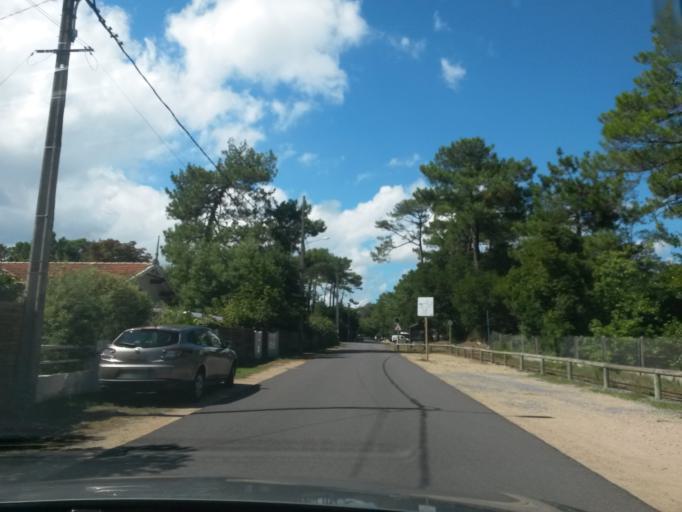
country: FR
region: Aquitaine
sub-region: Departement de la Gironde
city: Arcachon
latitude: 44.6577
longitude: -1.2436
